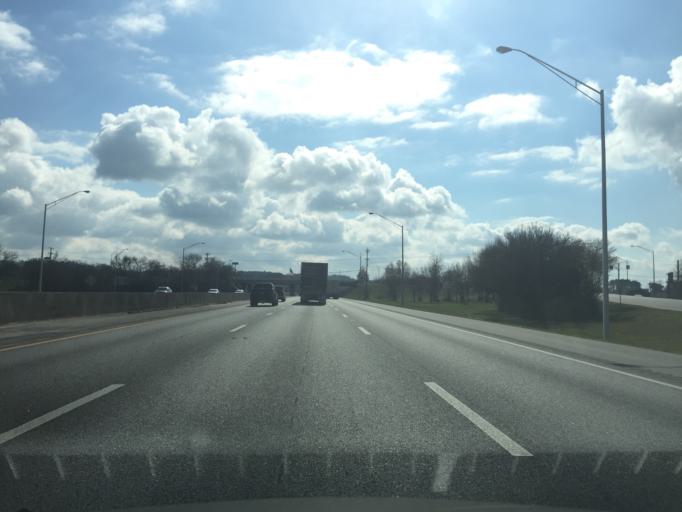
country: US
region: Tennessee
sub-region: Hamilton County
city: East Ridge
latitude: 34.9921
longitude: -85.2054
